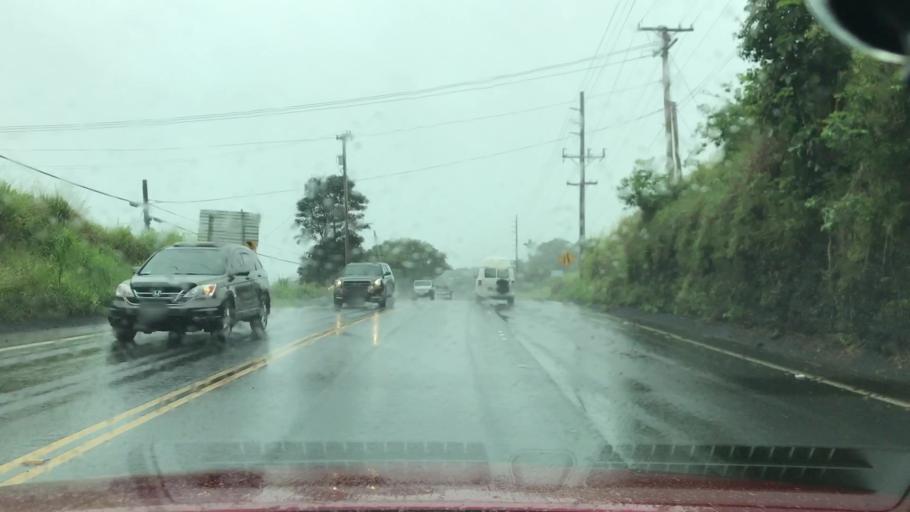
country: US
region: Hawaii
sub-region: Hawaii County
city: Pepeekeo
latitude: 19.9880
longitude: -155.2434
